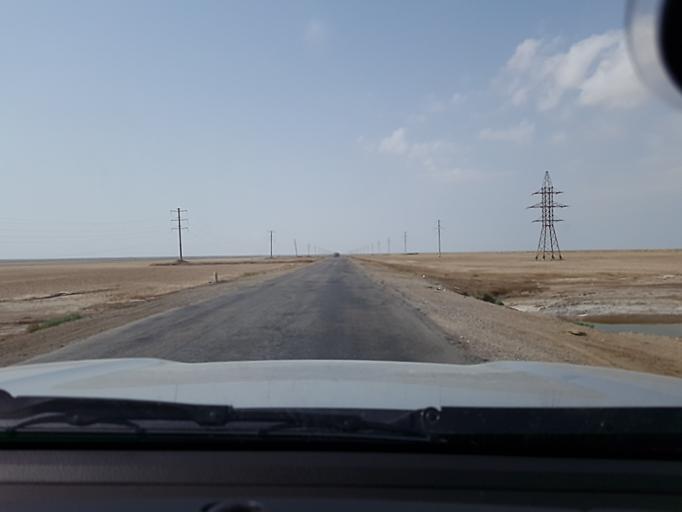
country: TM
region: Balkan
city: Gumdag
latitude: 39.0826
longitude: 54.5842
